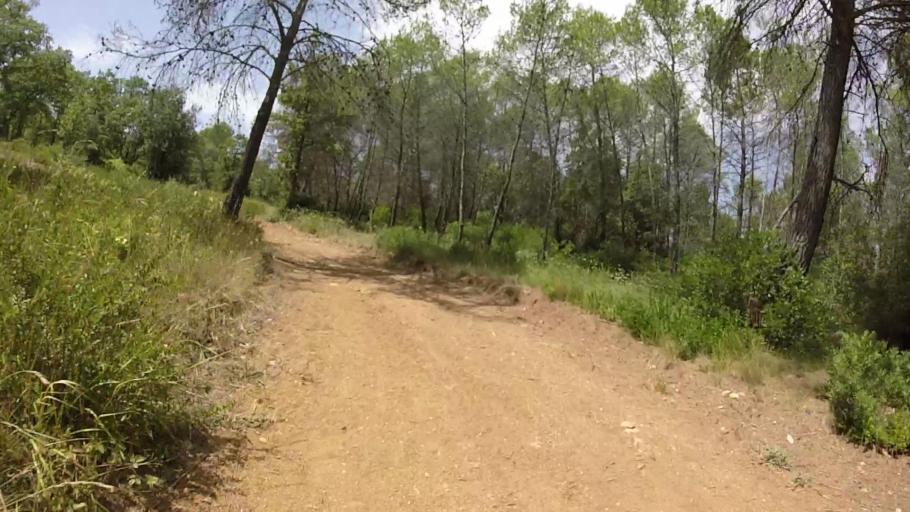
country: FR
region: Provence-Alpes-Cote d'Azur
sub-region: Departement des Alpes-Maritimes
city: Mougins
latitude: 43.6169
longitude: 7.0348
